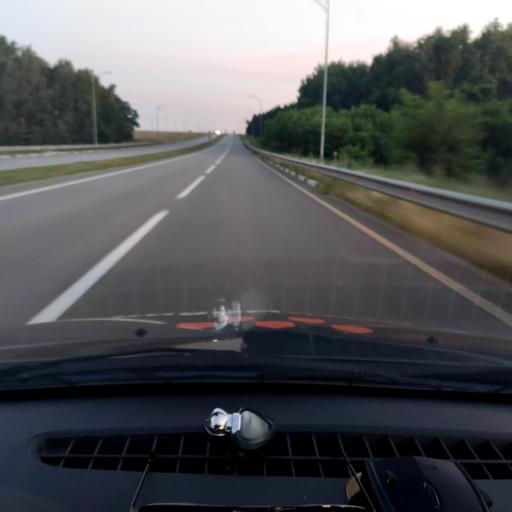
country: RU
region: Belgorod
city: Staryy Oskol
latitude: 51.4031
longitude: 37.8774
